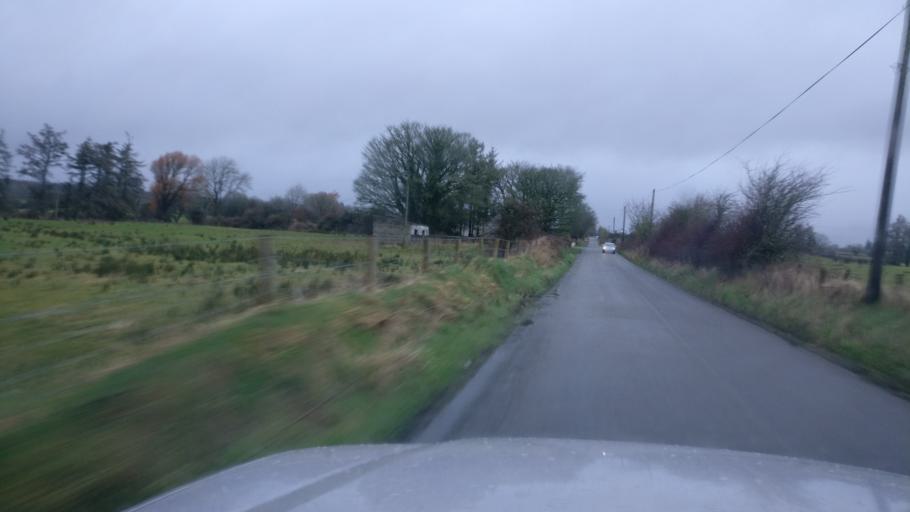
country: IE
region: Connaught
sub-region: County Galway
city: Loughrea
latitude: 53.2643
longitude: -8.4049
